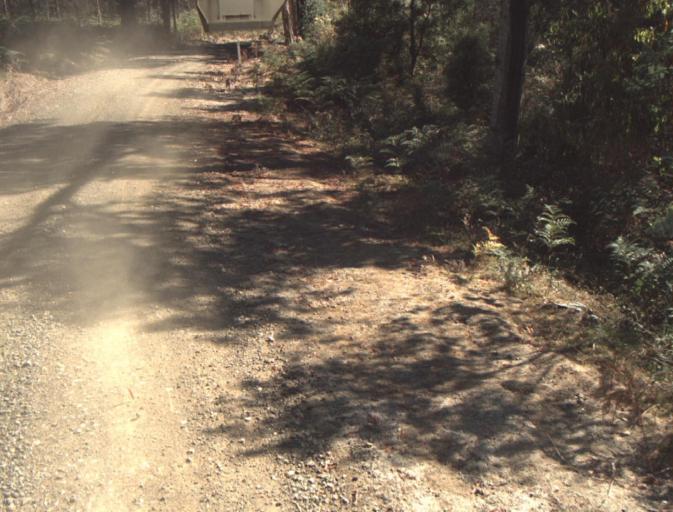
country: AU
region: Tasmania
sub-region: Dorset
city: Scottsdale
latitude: -41.2725
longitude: 147.3752
